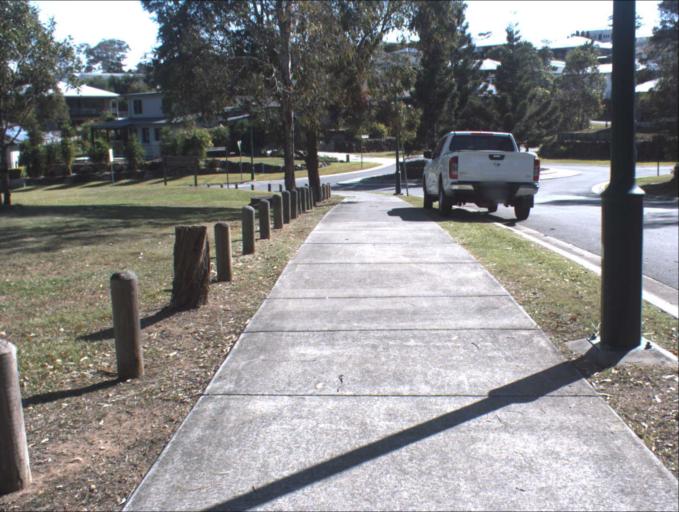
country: AU
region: Queensland
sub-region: Logan
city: Slacks Creek
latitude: -27.6329
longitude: 153.1584
